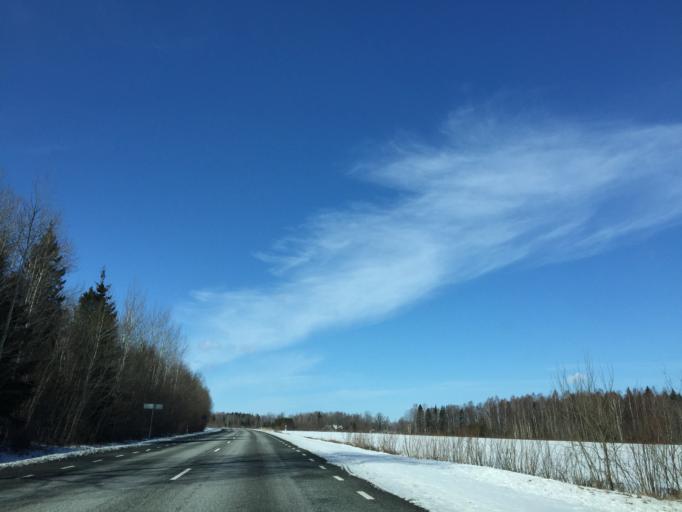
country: EE
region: Paernumaa
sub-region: Audru vald
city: Audru
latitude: 58.4775
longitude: 24.1788
